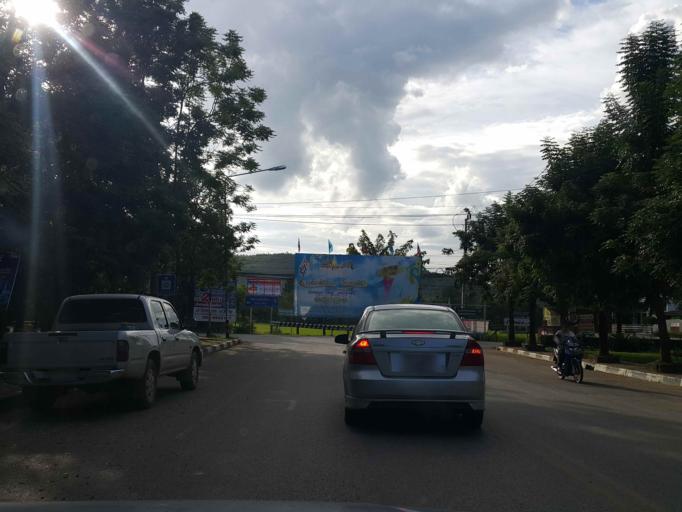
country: TH
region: Sukhothai
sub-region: Amphoe Si Satchanalai
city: Si Satchanalai
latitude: 17.5178
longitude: 99.7575
